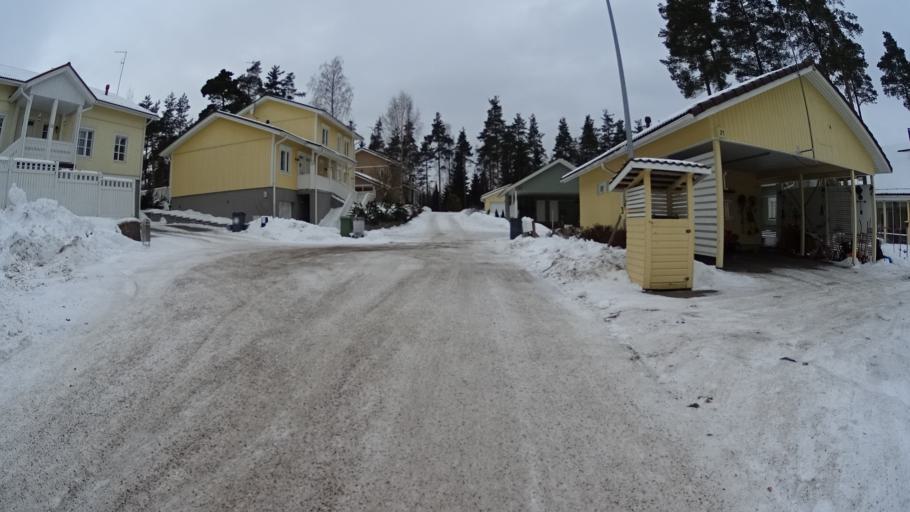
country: FI
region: Uusimaa
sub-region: Helsinki
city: Espoo
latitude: 60.2209
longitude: 24.6246
